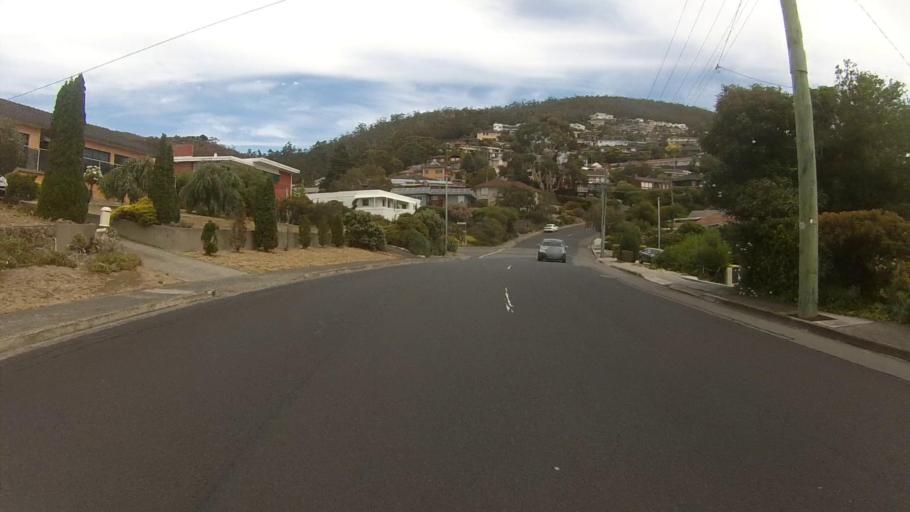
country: AU
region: Tasmania
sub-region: Kingborough
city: Taroona
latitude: -42.9189
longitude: 147.3554
